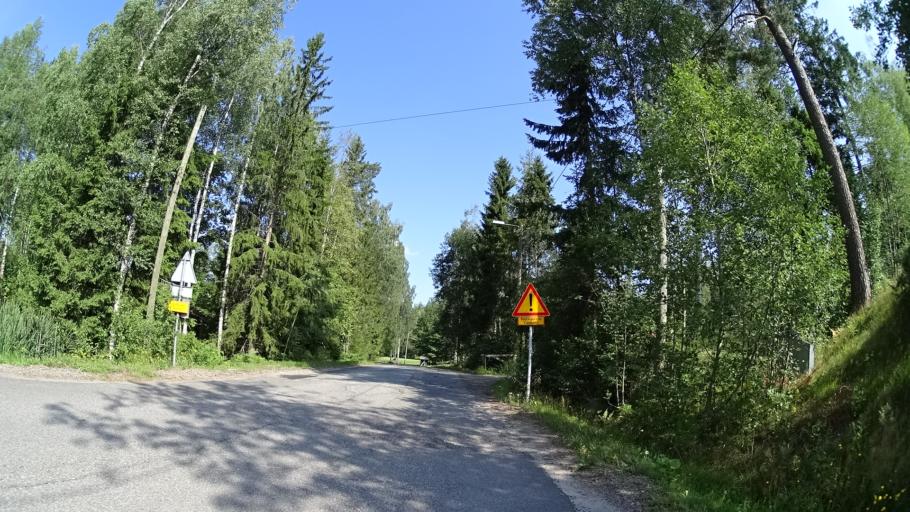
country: FI
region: Uusimaa
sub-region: Helsinki
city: Kilo
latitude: 60.3235
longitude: 24.8090
